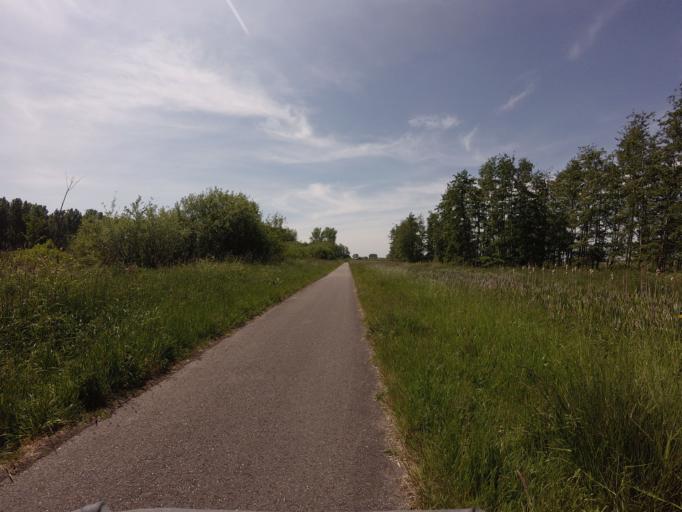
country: NL
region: Utrecht
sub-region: Gemeente Houten
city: Houten
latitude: 52.0046
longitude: 5.1536
